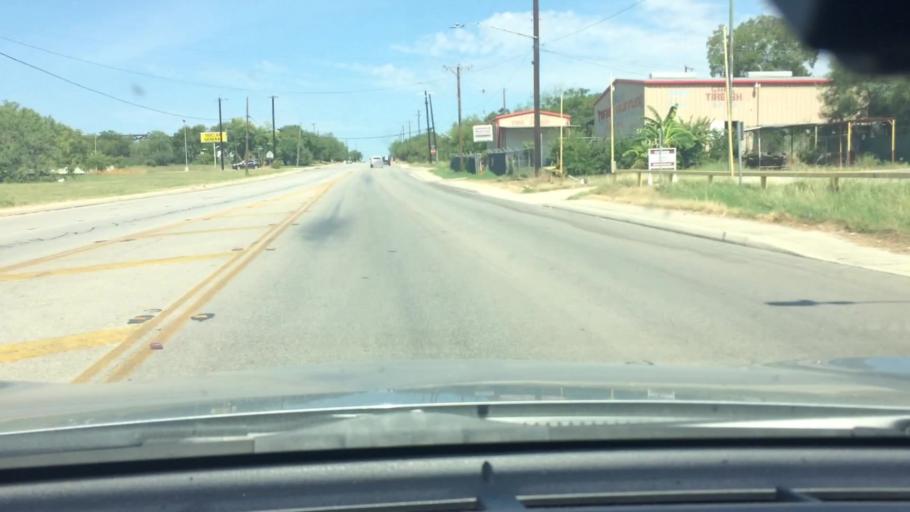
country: US
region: Texas
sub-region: Bexar County
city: San Antonio
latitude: 29.3988
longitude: -98.4376
